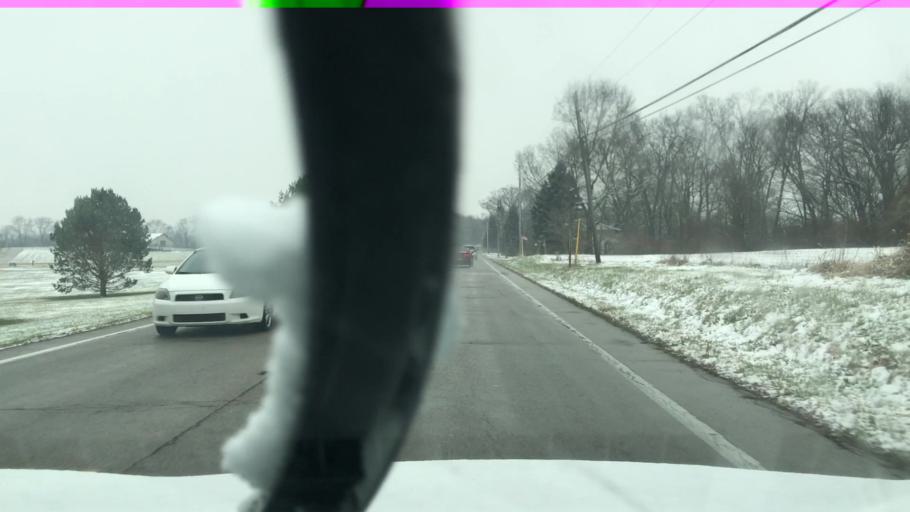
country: US
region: Indiana
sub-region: Delaware County
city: Yorktown
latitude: 40.1572
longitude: -85.5320
